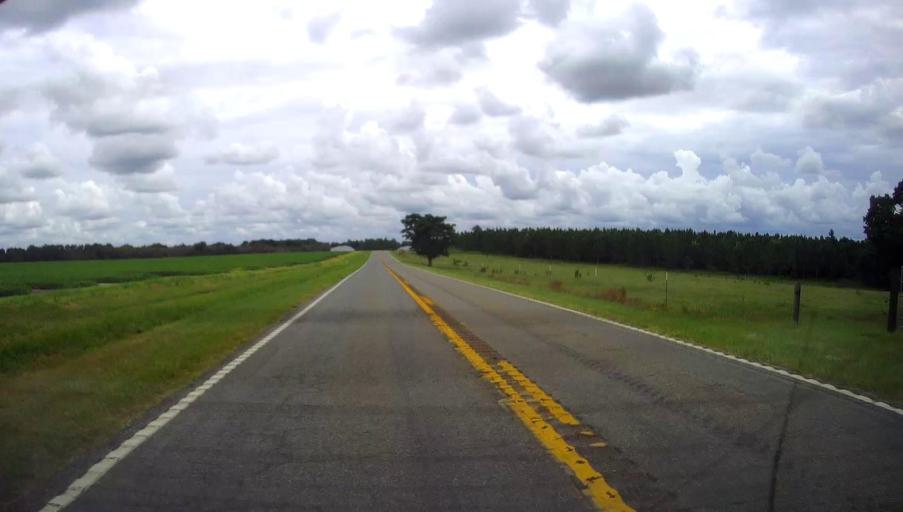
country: US
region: Georgia
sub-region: Dooly County
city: Unadilla
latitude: 32.2626
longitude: -83.8088
